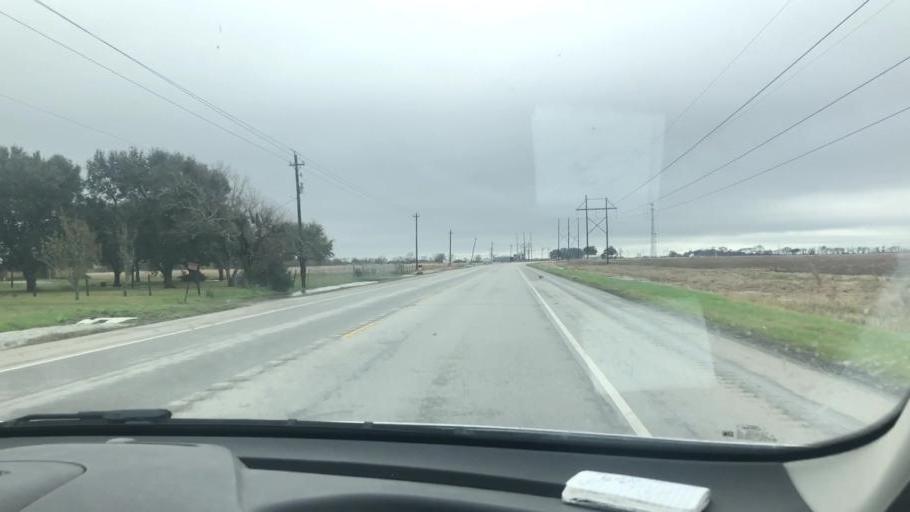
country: US
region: Texas
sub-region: Wharton County
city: Boling
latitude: 29.1473
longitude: -95.9881
